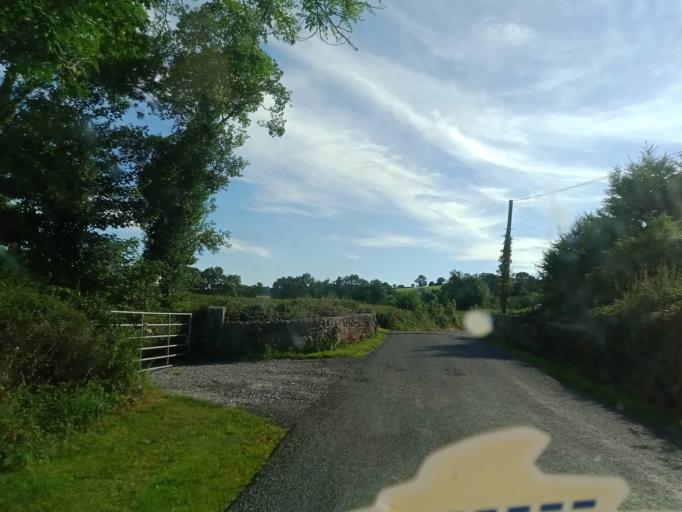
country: IE
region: Leinster
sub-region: Kilkenny
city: Ballyragget
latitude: 52.7711
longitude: -7.3902
